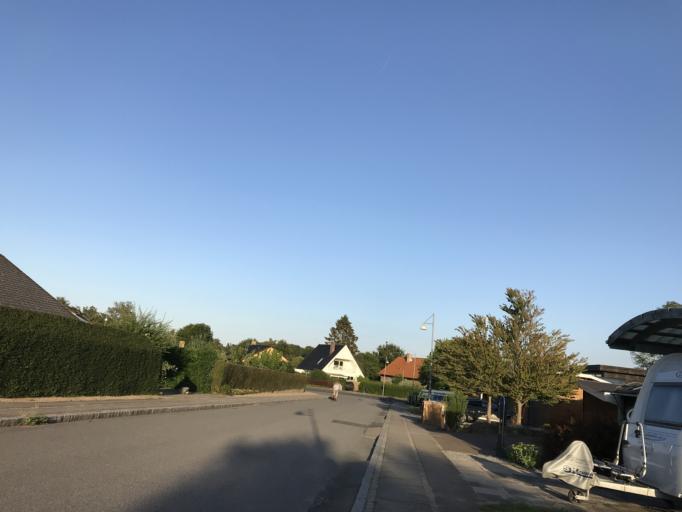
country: DK
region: South Denmark
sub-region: Middelfart Kommune
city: Middelfart
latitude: 55.4974
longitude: 9.7172
